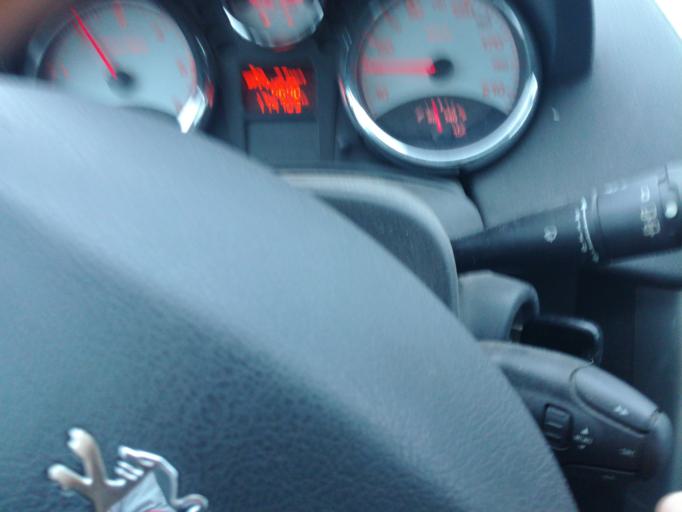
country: FR
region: Provence-Alpes-Cote d'Azur
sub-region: Departement du Var
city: Puget-sur-Argens
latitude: 43.4392
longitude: 6.7077
